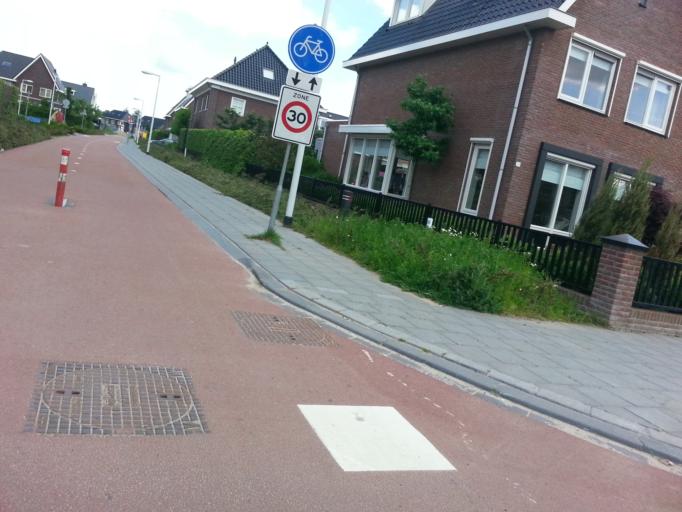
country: NL
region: Gelderland
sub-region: Gemeente Barneveld
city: Barneveld
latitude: 52.1273
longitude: 5.5931
